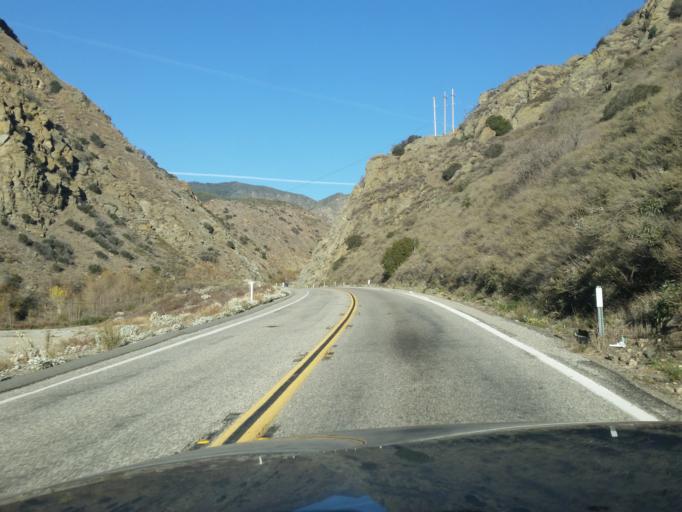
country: US
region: California
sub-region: San Bernardino County
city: Yucaipa
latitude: 34.0890
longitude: -117.0389
